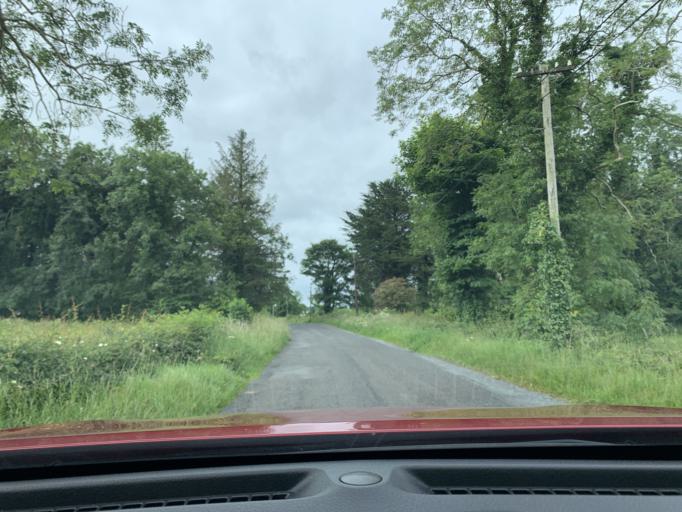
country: IE
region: Connaught
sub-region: Sligo
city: Sligo
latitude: 54.3246
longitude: -8.4746
